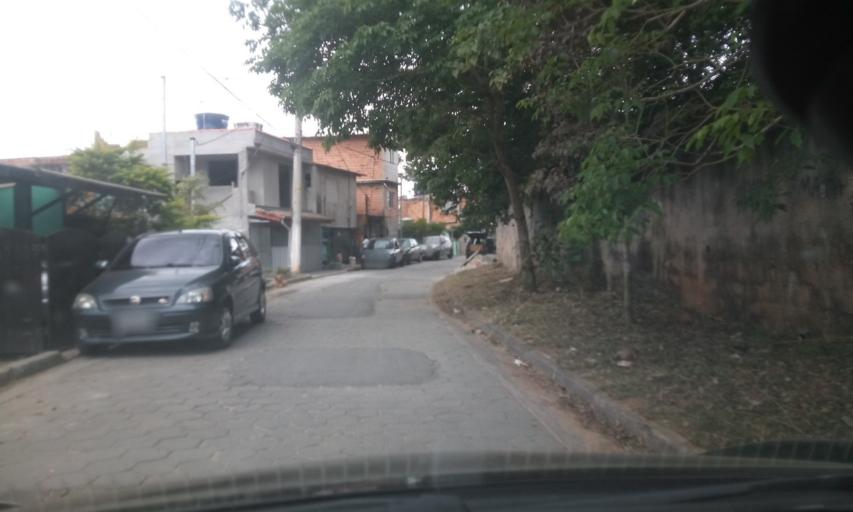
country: BR
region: Sao Paulo
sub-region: Diadema
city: Diadema
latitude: -23.7682
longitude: -46.6109
